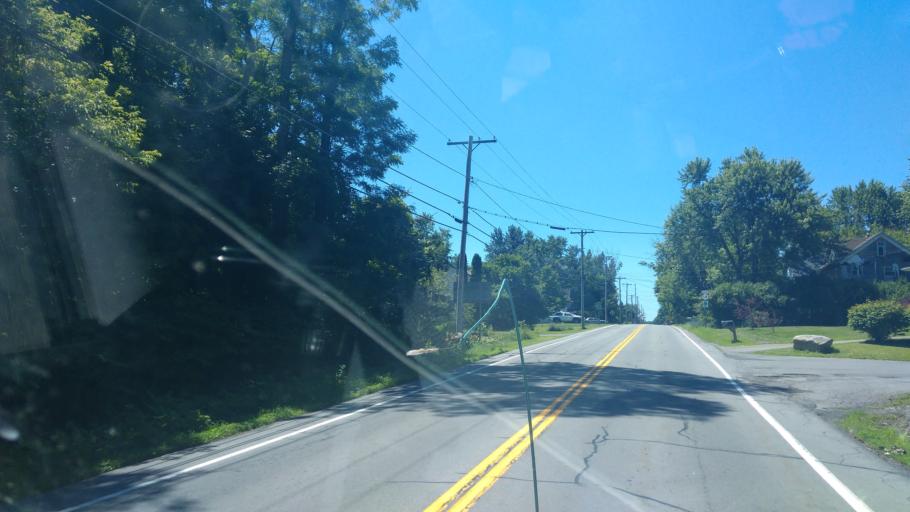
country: US
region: New York
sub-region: Wayne County
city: Sodus
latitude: 43.2059
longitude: -76.9824
